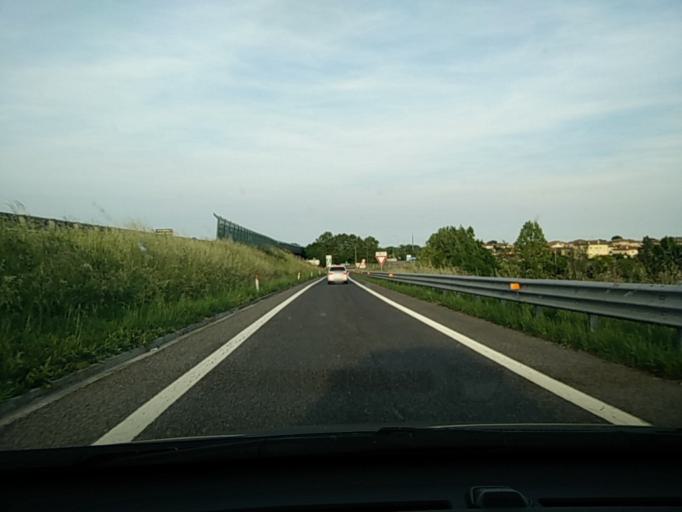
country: IT
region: Veneto
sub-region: Provincia di Venezia
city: Dese
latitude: 45.5343
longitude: 12.2988
